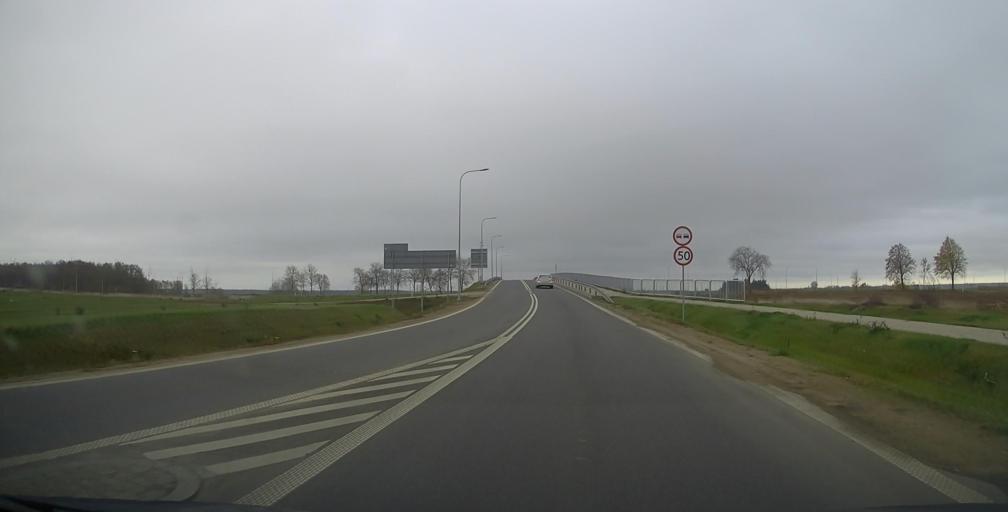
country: PL
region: Podlasie
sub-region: Powiat grajewski
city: Rajgrod
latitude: 53.8589
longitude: 22.5831
